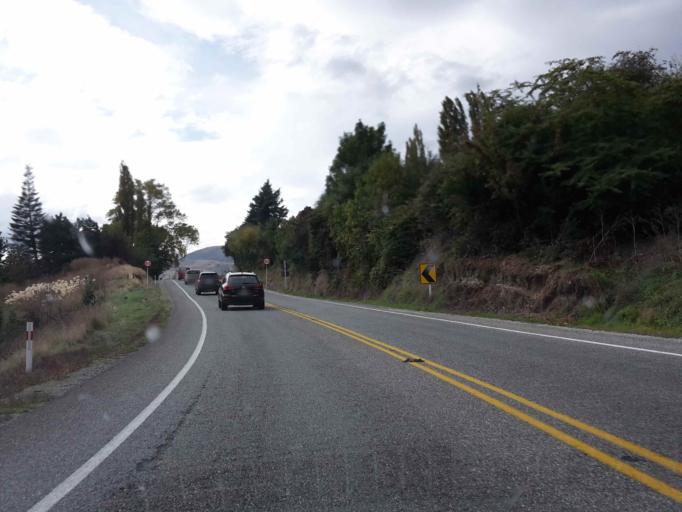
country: NZ
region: Otago
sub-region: Queenstown-Lakes District
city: Arrowtown
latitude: -44.9951
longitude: 168.8044
